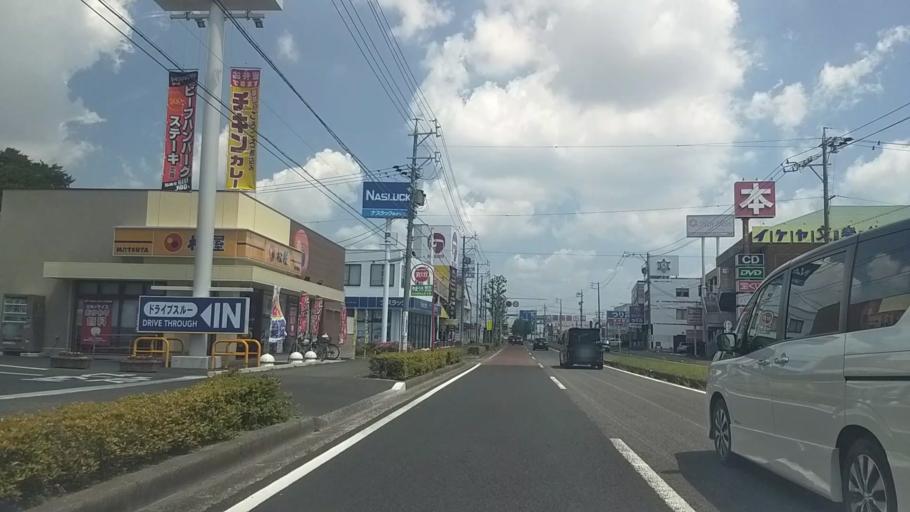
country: JP
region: Shizuoka
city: Hamamatsu
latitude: 34.7298
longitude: 137.7328
